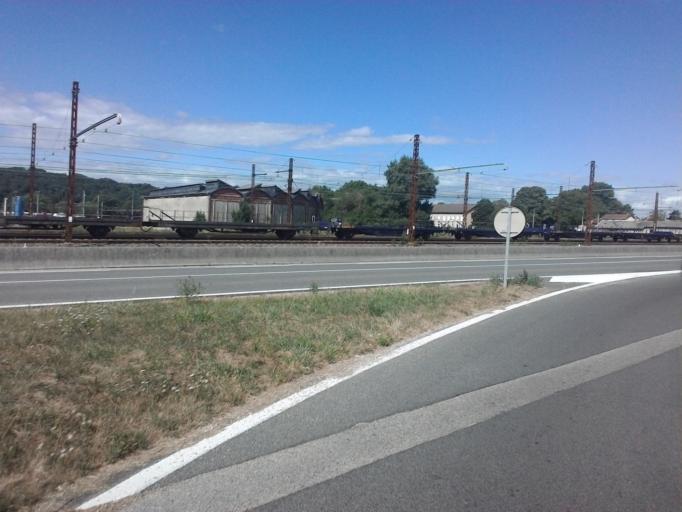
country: FR
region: Rhone-Alpes
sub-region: Departement de l'Ain
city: Amberieu-en-Bugey
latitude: 45.9538
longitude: 5.3548
